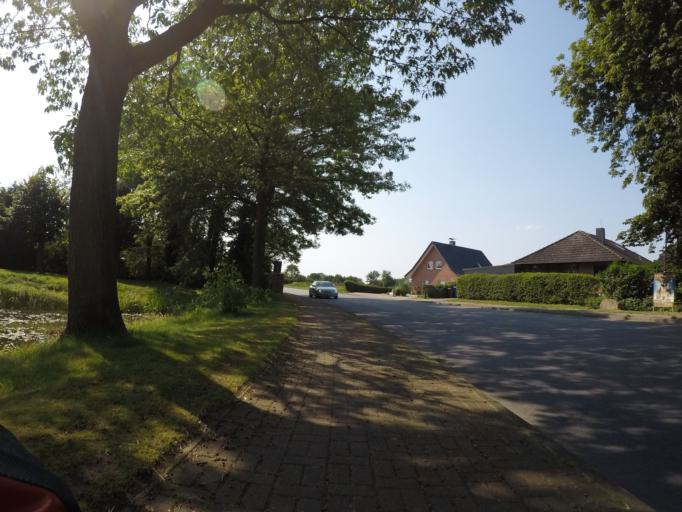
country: DE
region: Schleswig-Holstein
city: Sievershutten
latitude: 53.8428
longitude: 10.1014
